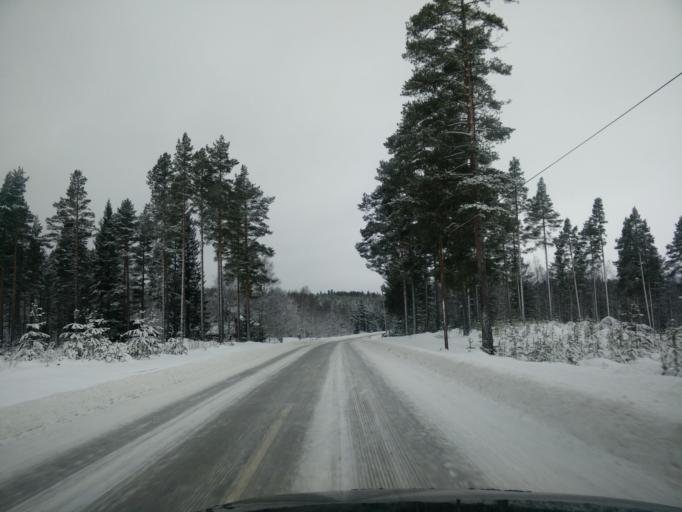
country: SE
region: Vaesternorrland
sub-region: Ange Kommun
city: Ange
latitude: 62.3937
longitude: 15.3871
